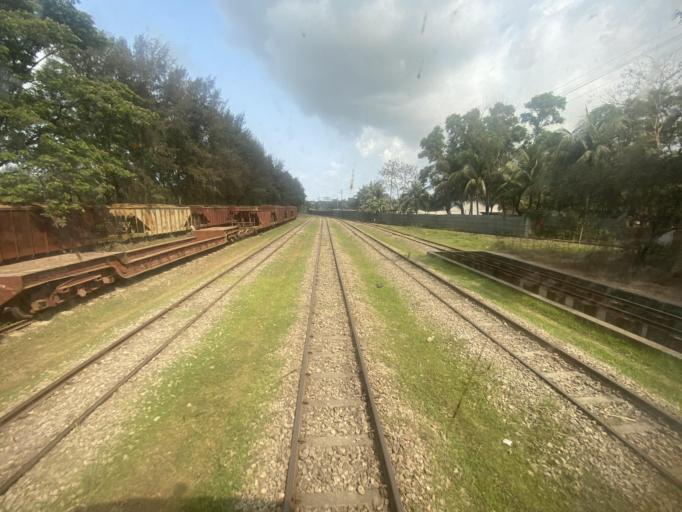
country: BD
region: Chittagong
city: Chittagong
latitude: 22.3242
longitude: 91.7796
